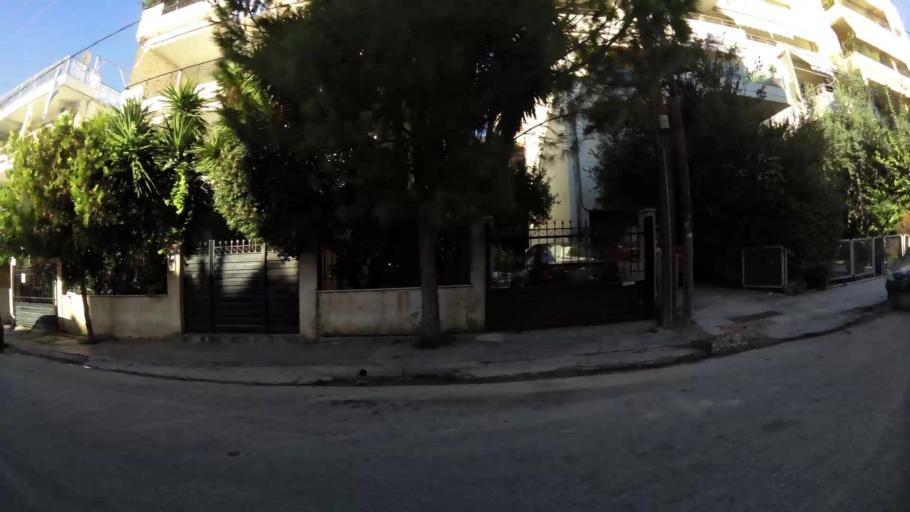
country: GR
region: Attica
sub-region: Nomarchia Anatolikis Attikis
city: Pallini
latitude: 37.9998
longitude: 23.8759
